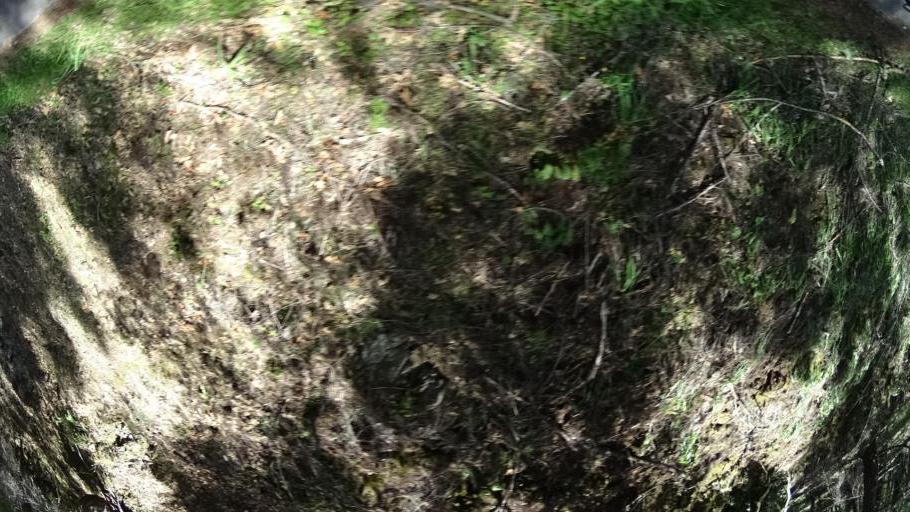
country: US
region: California
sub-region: Humboldt County
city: Redway
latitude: 40.1932
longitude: -123.5269
